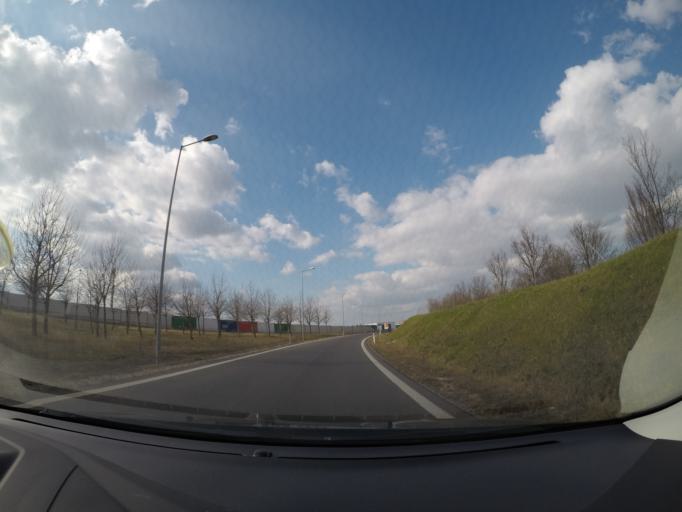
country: AT
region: Lower Austria
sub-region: Politischer Bezirk Modling
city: Vosendorf
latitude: 48.1330
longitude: 16.3415
